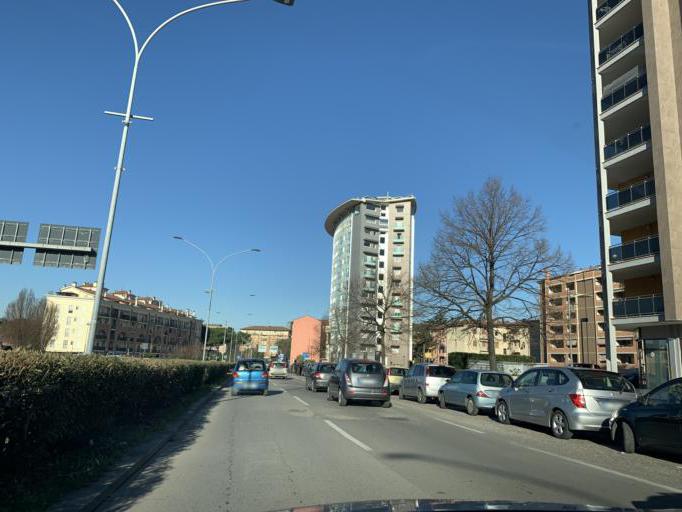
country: IT
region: Umbria
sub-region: Provincia di Terni
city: Terni
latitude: 42.5596
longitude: 12.6545
